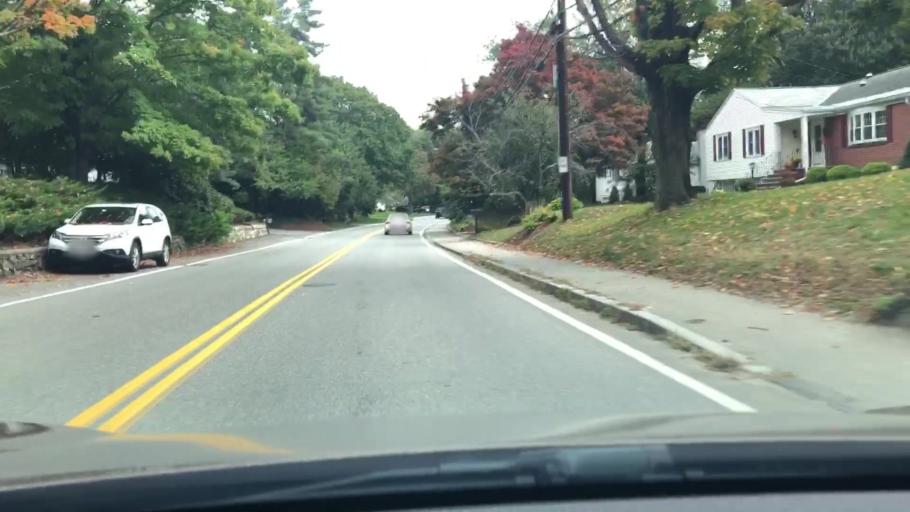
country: US
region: Massachusetts
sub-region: Middlesex County
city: Arlington
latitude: 42.4431
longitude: -71.1715
